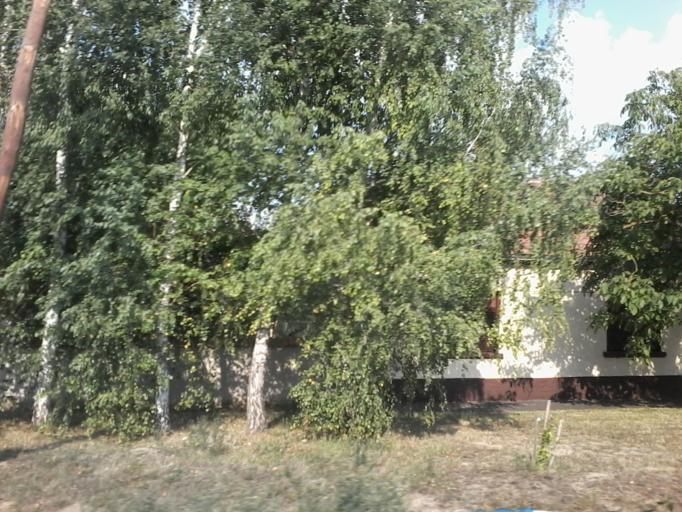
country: HU
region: Vas
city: Celldomolk
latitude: 47.2201
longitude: 17.0895
